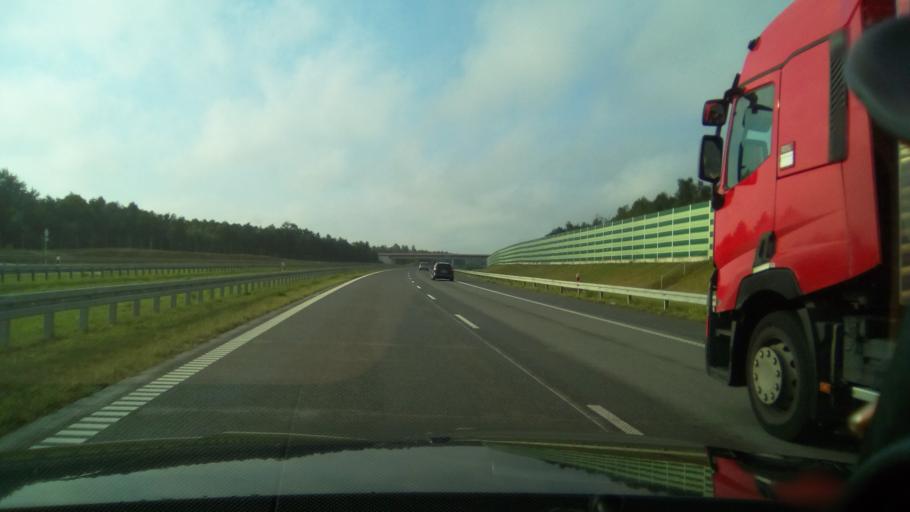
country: PL
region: Silesian Voivodeship
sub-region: Powiat czestochowski
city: Konopiska
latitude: 50.7334
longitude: 19.0563
